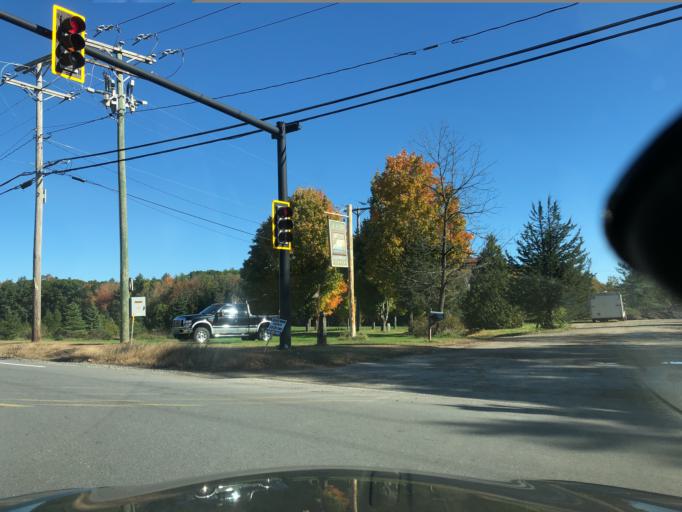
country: US
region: New Hampshire
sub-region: Rockingham County
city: Stratham Station
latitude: 43.0427
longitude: -70.9308
